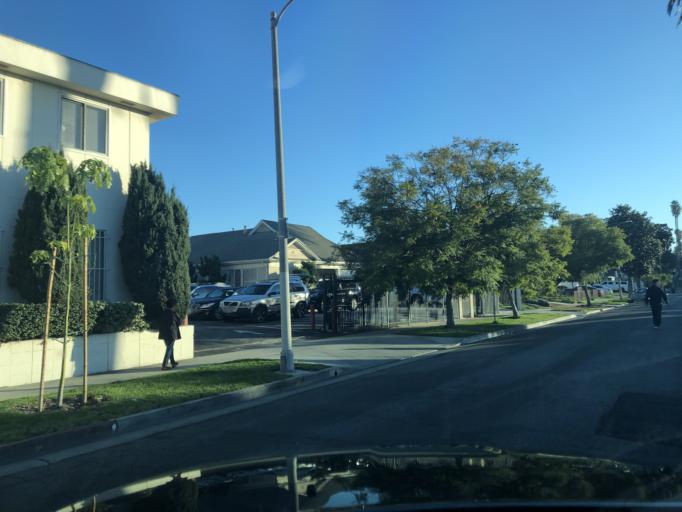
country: US
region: California
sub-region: Los Angeles County
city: Hollywood
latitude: 34.0523
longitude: -118.3166
